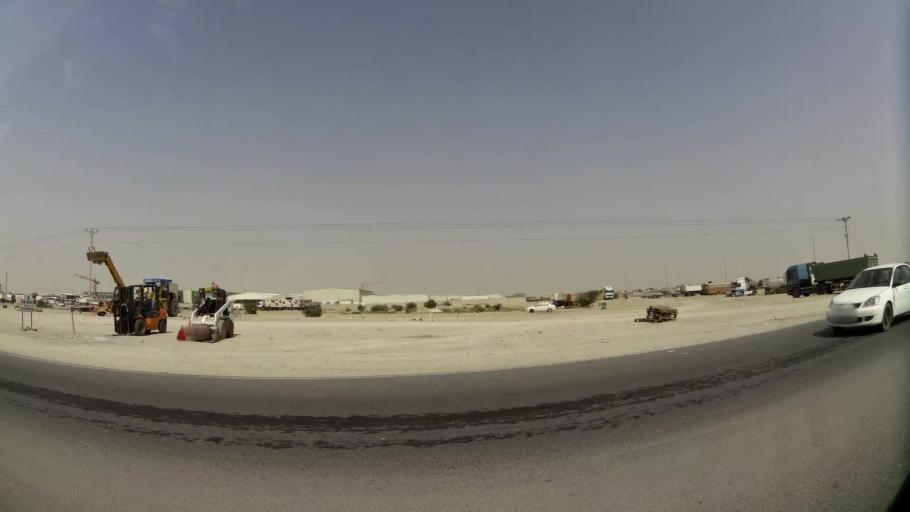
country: QA
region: Baladiyat ar Rayyan
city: Ar Rayyan
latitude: 25.1999
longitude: 51.3664
